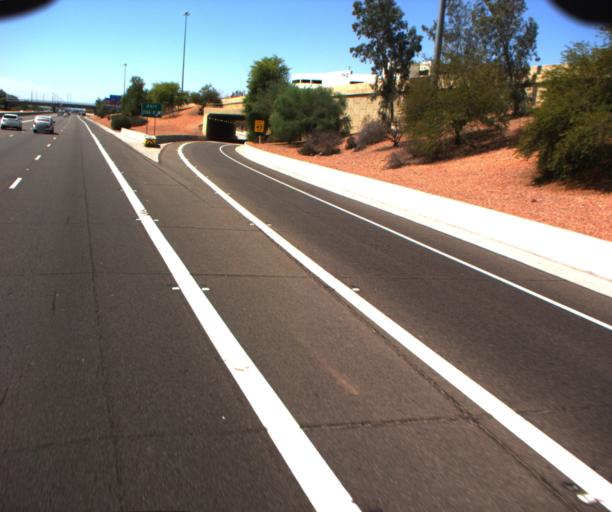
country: US
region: Arizona
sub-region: Maricopa County
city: Glendale
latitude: 33.6668
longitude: -112.1137
